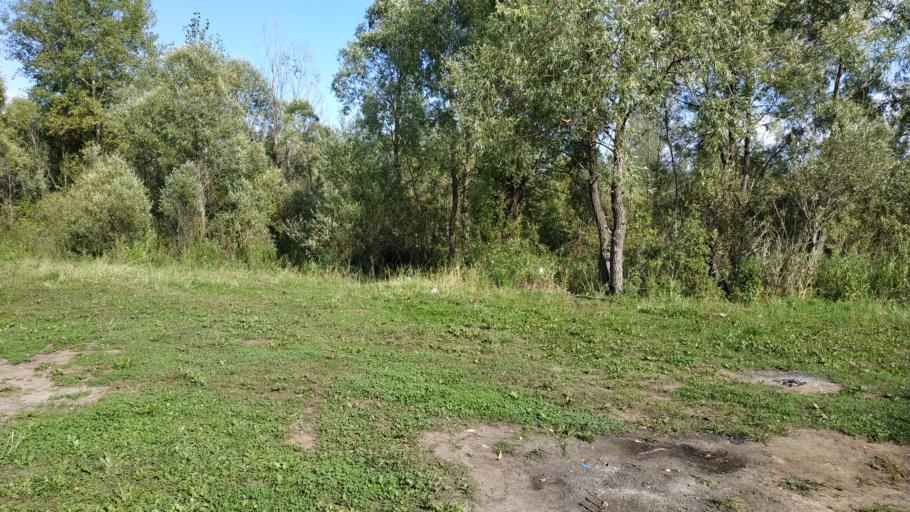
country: RU
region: Tatarstan
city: Nizhnekamsk
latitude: 55.6540
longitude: 51.7105
